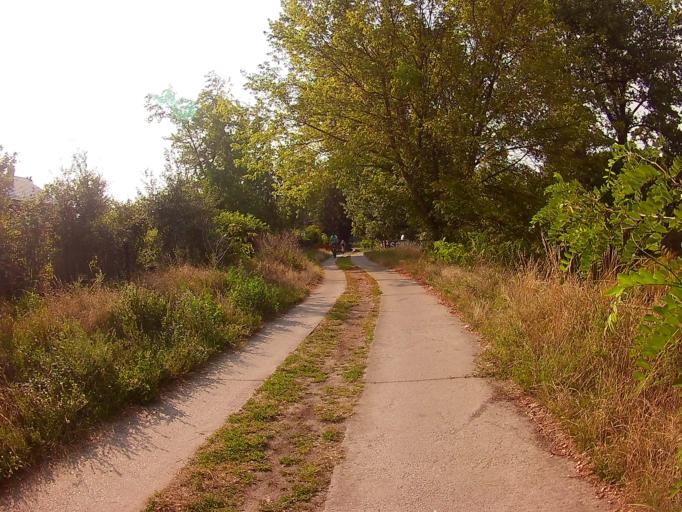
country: DE
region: Berlin
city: Biesdorf
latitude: 52.4781
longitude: 13.5646
